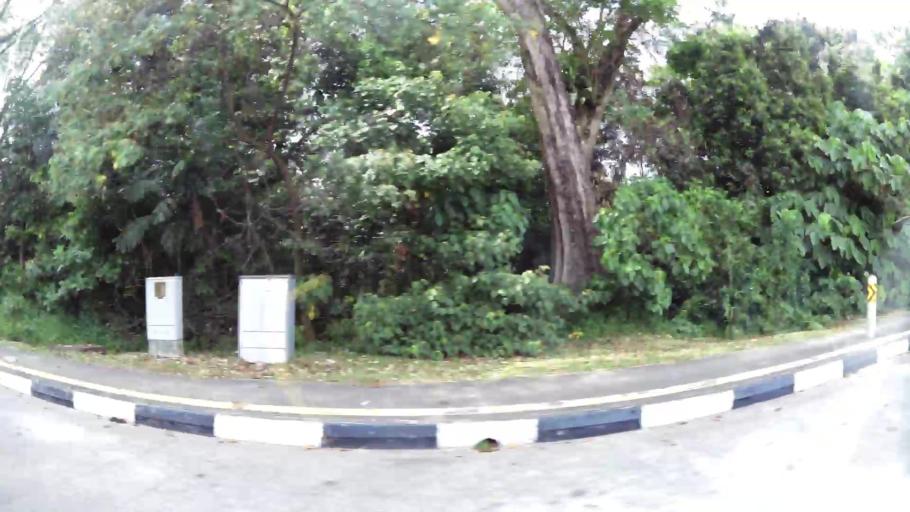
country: MY
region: Johor
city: Johor Bahru
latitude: 1.4216
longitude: 103.7557
